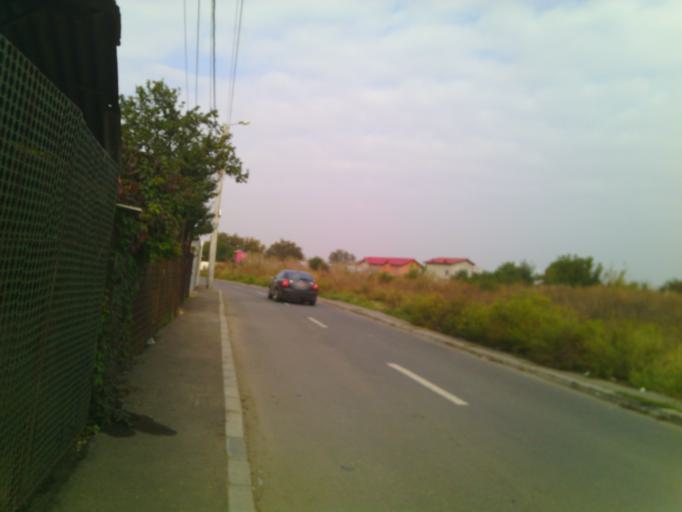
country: RO
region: Bucuresti
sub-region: Municipiul Bucuresti
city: Bucuresti
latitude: 44.3877
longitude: 26.0723
